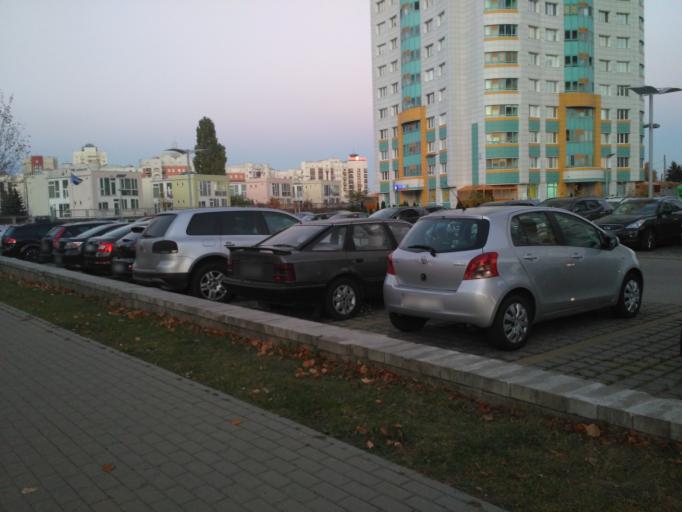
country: BY
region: Minsk
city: Novoye Medvezhino
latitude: 53.8677
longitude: 27.4852
